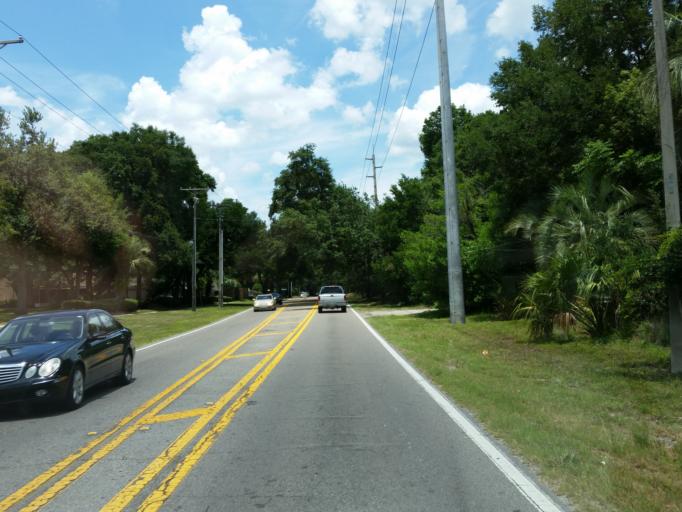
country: US
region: Florida
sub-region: Hillsborough County
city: Valrico
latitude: 27.9409
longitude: -82.2528
